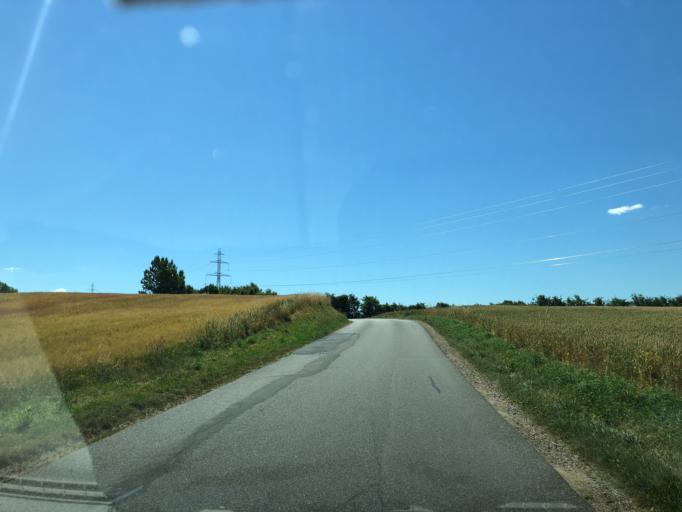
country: DK
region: Central Jutland
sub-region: Viborg Kommune
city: Viborg
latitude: 56.5132
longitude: 9.5067
